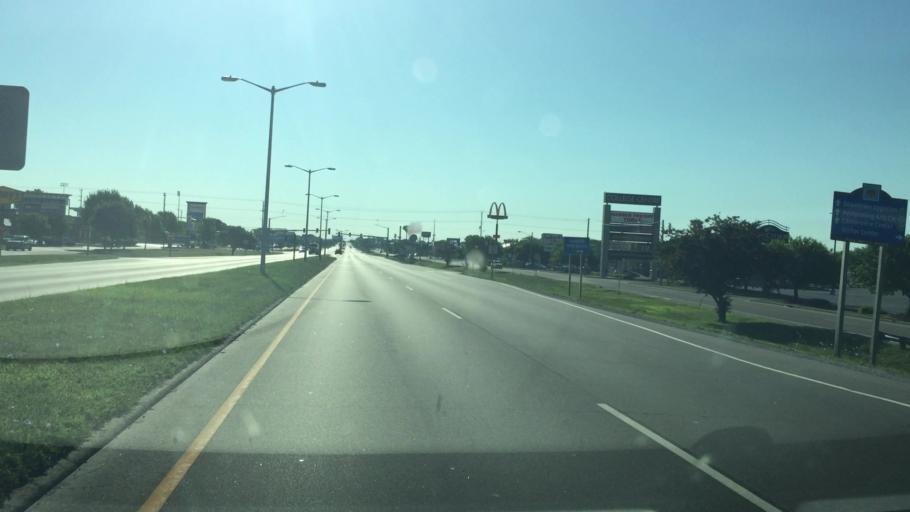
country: US
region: Wisconsin
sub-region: Outagamie County
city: Appleton
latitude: 44.2618
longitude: -88.4595
